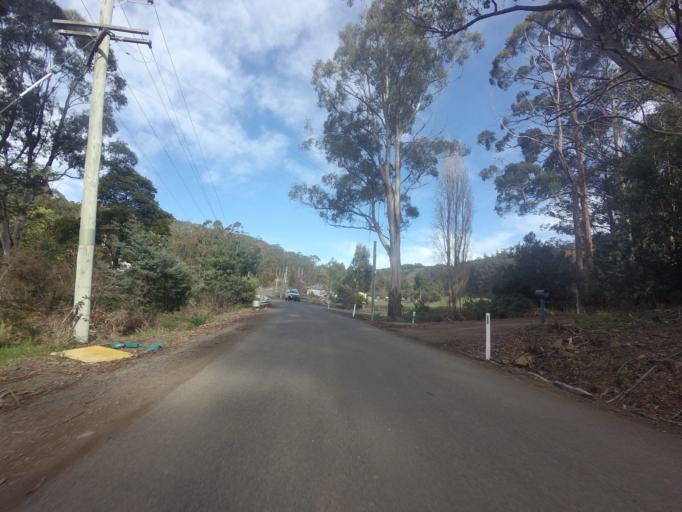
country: AU
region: Tasmania
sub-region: Kingborough
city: Margate
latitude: -42.9872
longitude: 147.1923
